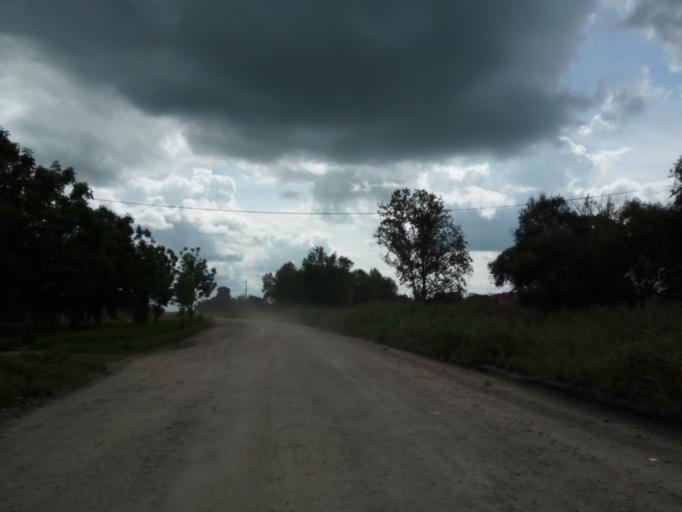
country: RU
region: Primorskiy
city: Dal'nerechensk
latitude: 45.9491
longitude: 133.8244
